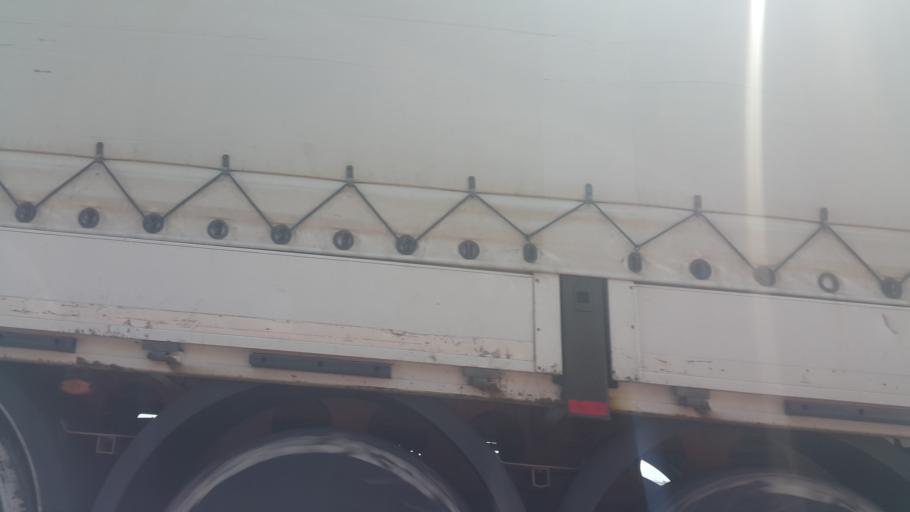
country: TR
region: Hatay
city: Serinyol
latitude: 36.3800
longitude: 36.2288
